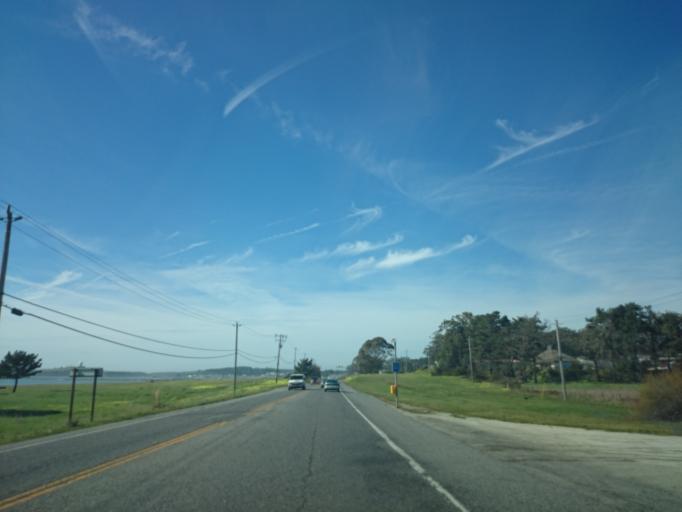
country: US
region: California
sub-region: San Mateo County
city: El Granada
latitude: 37.4976
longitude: -122.4616
